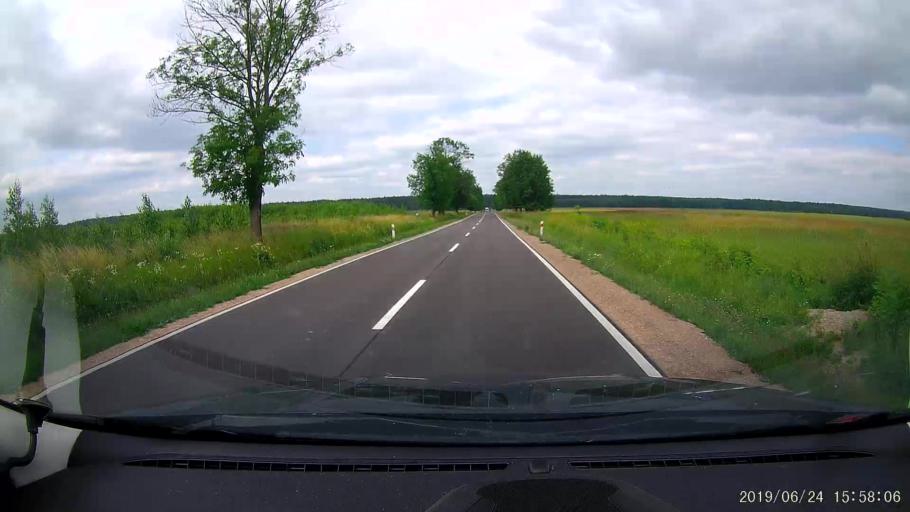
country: PL
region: Subcarpathian Voivodeship
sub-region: Powiat lubaczowski
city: Cieszanow
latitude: 50.2577
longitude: 23.1421
